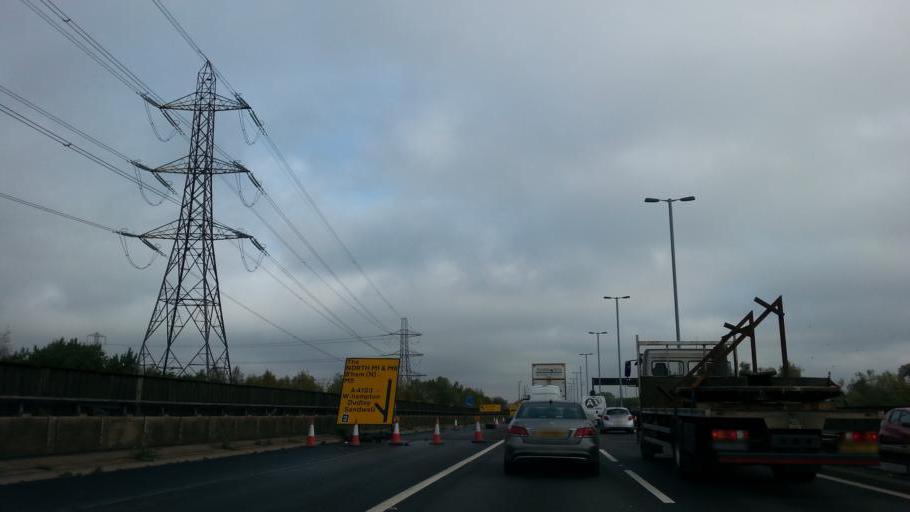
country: GB
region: England
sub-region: Sandwell
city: Oldbury
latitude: 52.4870
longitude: -2.0239
